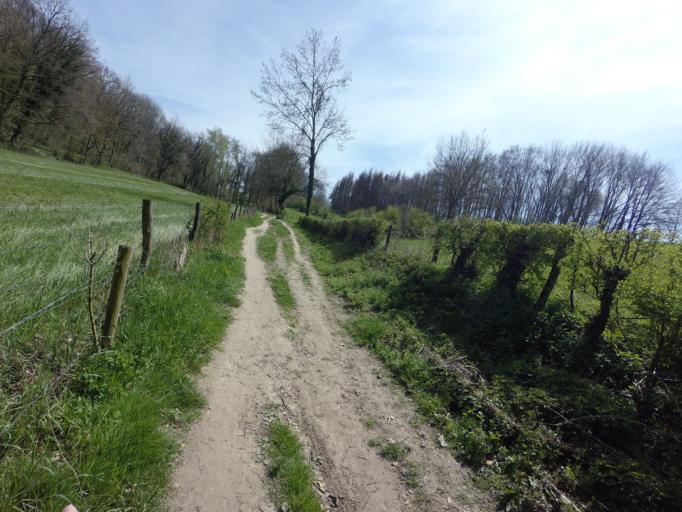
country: NL
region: Limburg
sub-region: Eijsden-Margraten
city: Eijsden
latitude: 50.7745
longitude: 5.7672
